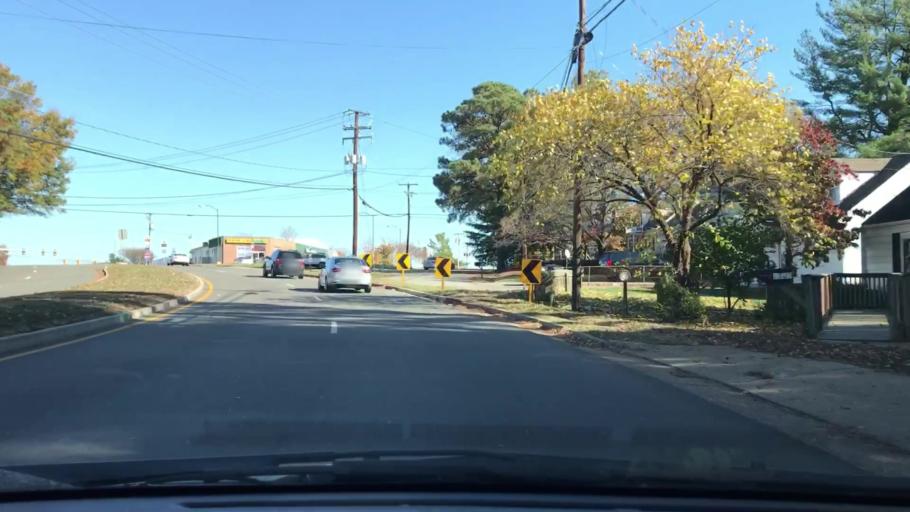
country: US
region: Virginia
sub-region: Henrico County
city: Laurel
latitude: 37.6291
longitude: -77.5379
